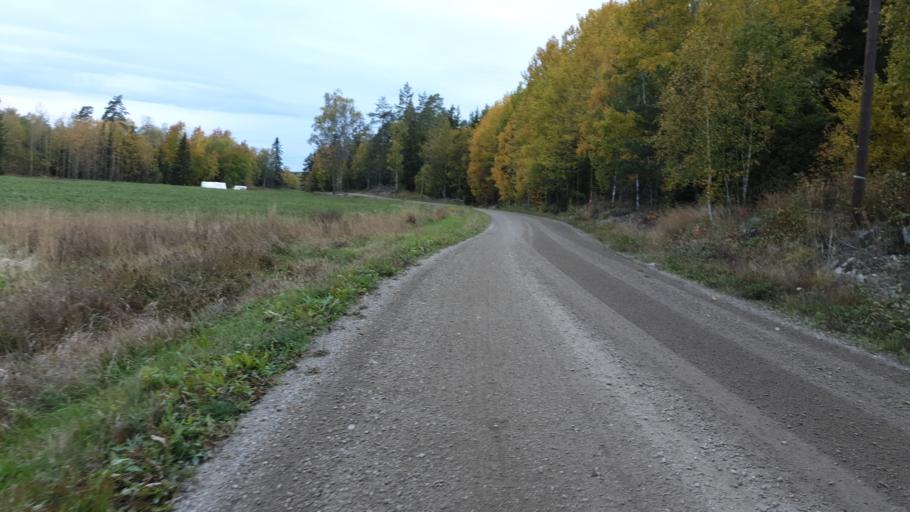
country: SE
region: Vaestmanland
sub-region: Sala Kommun
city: Sala
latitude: 59.8188
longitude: 16.6505
